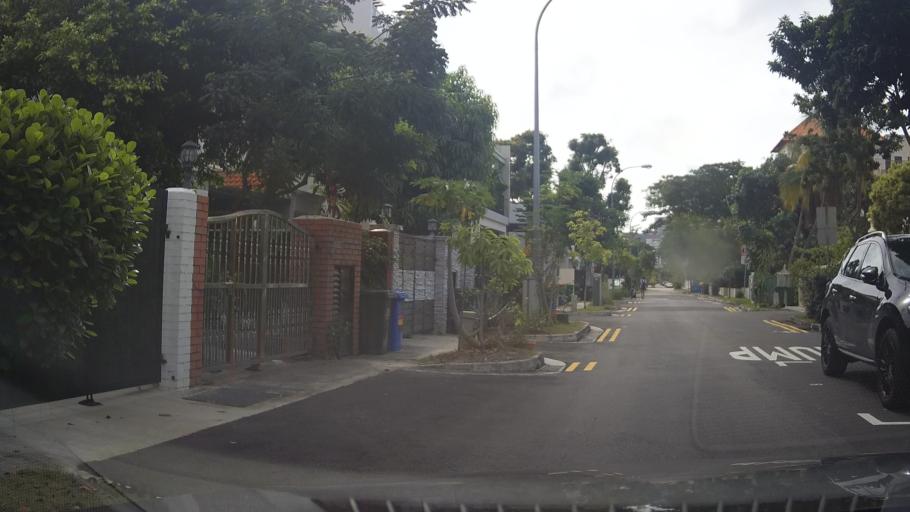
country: SG
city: Singapore
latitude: 1.3110
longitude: 103.8989
